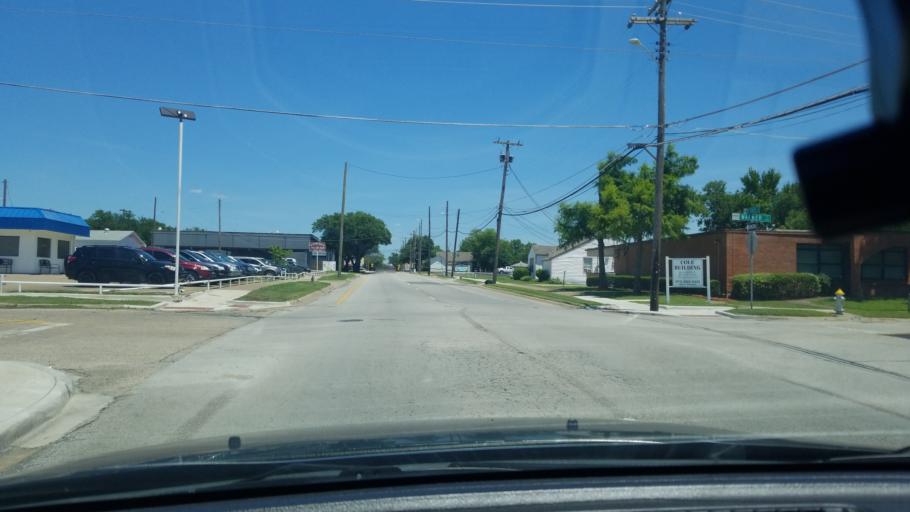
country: US
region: Texas
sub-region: Dallas County
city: Mesquite
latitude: 32.7668
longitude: -96.6045
